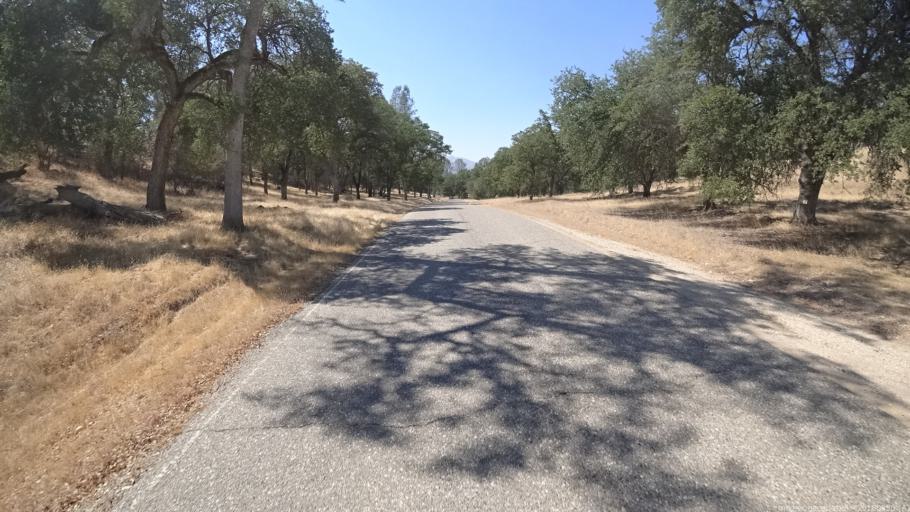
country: US
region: California
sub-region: Monterey County
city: Greenfield
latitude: 36.0809
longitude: -121.3865
